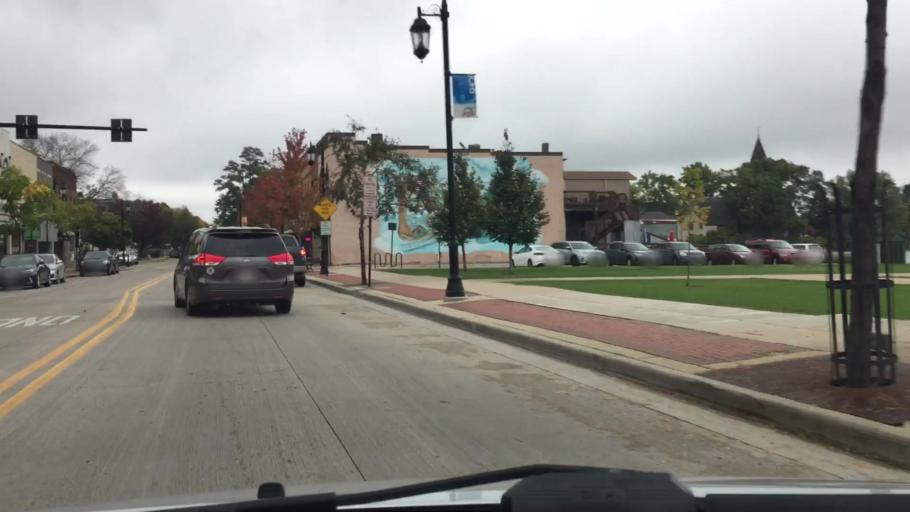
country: US
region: Wisconsin
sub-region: Waukesha County
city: Oconomowoc
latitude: 43.1116
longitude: -88.4994
